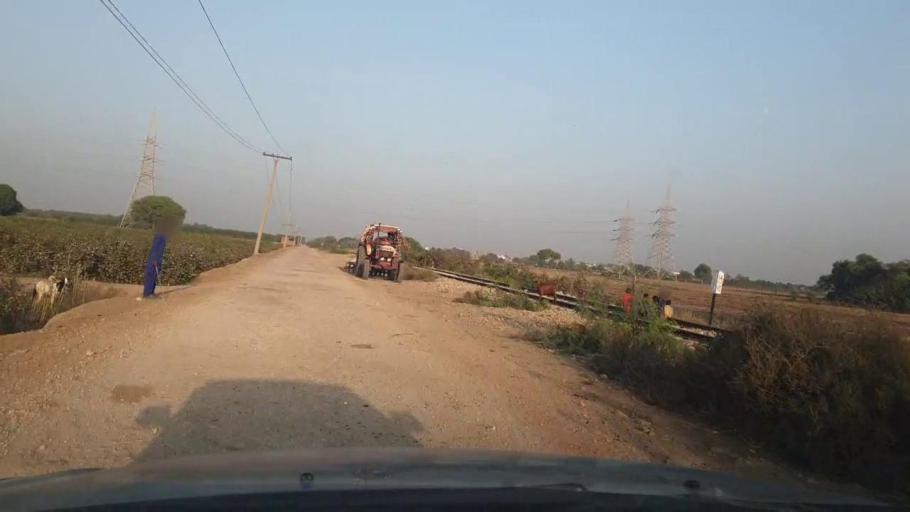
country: PK
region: Sindh
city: Tando Jam
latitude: 25.4254
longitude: 68.5107
